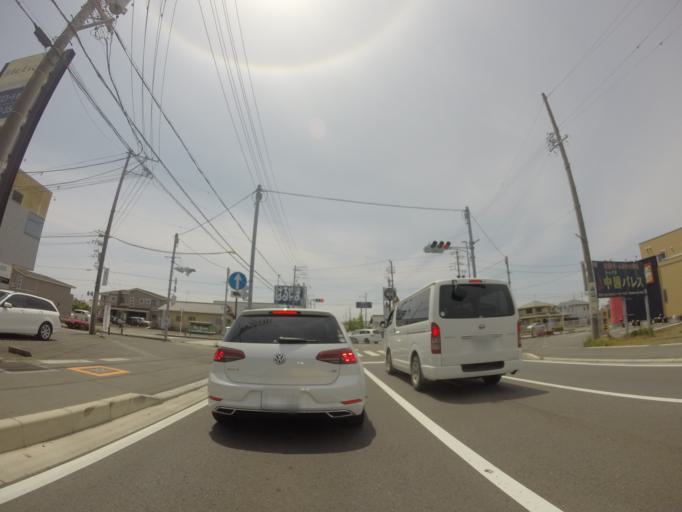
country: JP
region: Shizuoka
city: Yaizu
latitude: 34.8484
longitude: 138.3083
